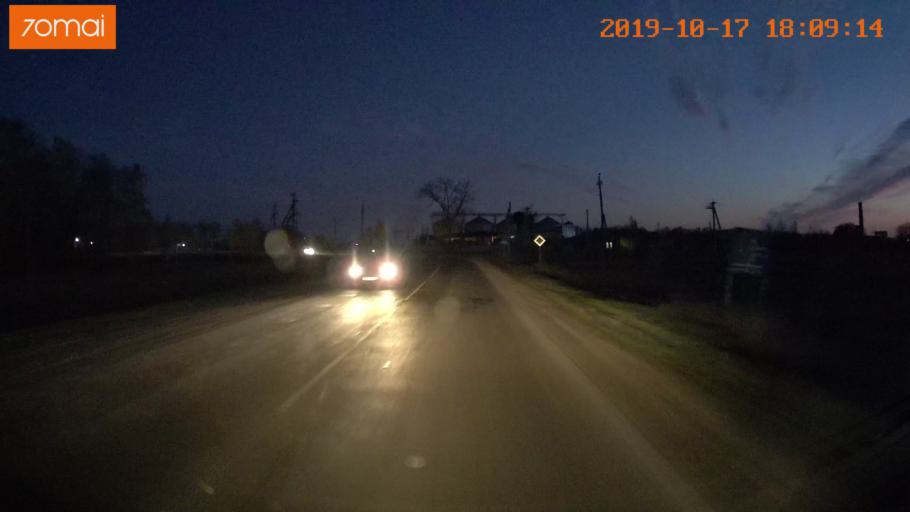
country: RU
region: Tula
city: Kurkino
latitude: 53.4244
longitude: 38.6445
